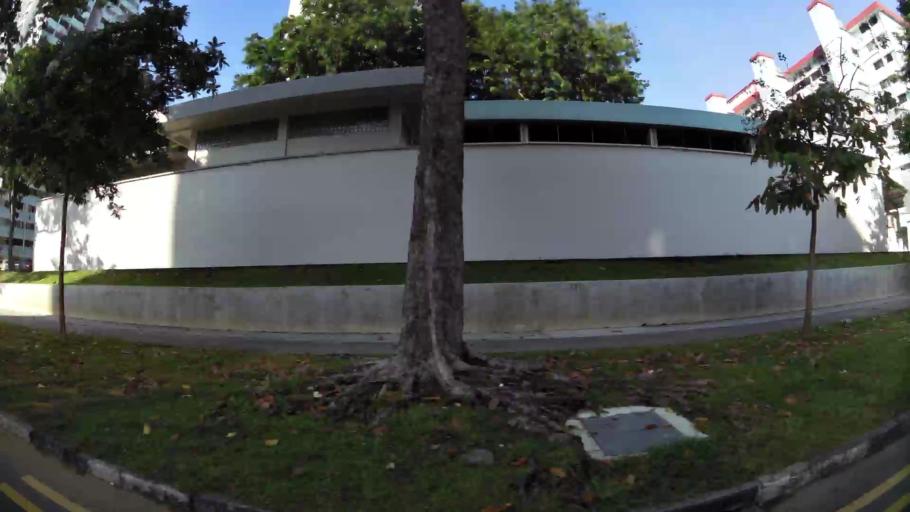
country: SG
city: Singapore
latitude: 1.3291
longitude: 103.9347
